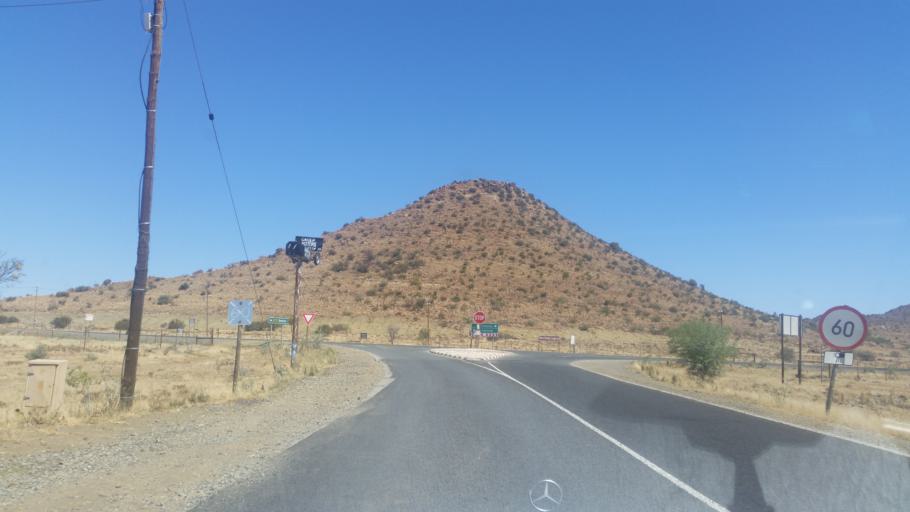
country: ZA
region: Northern Cape
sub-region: Pixley ka Seme District Municipality
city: Colesberg
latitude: -30.6326
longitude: 25.4516
